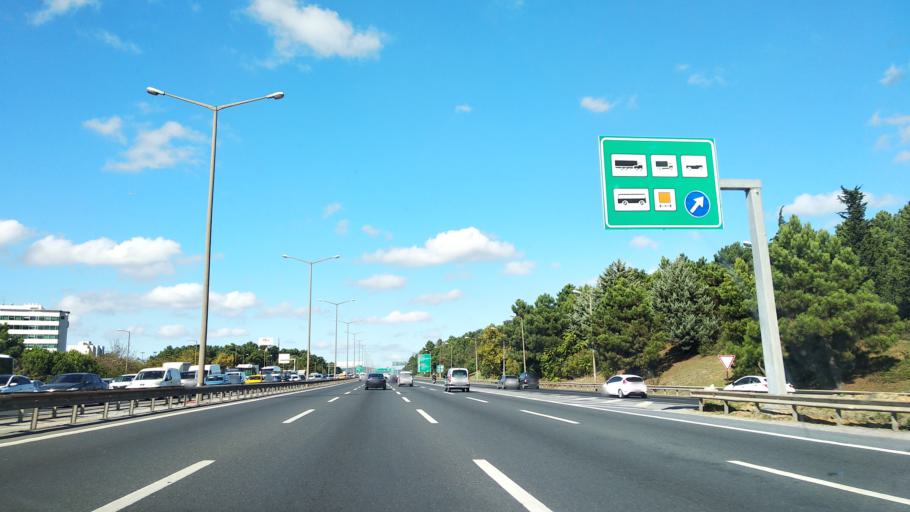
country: TR
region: Istanbul
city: Umraniye
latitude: 41.0338
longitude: 29.1212
